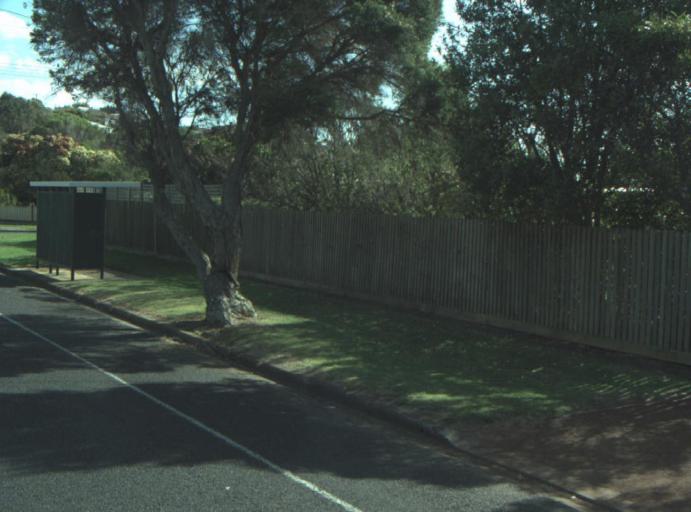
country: AU
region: Victoria
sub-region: Greater Geelong
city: Leopold
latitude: -38.2662
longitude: 144.5457
